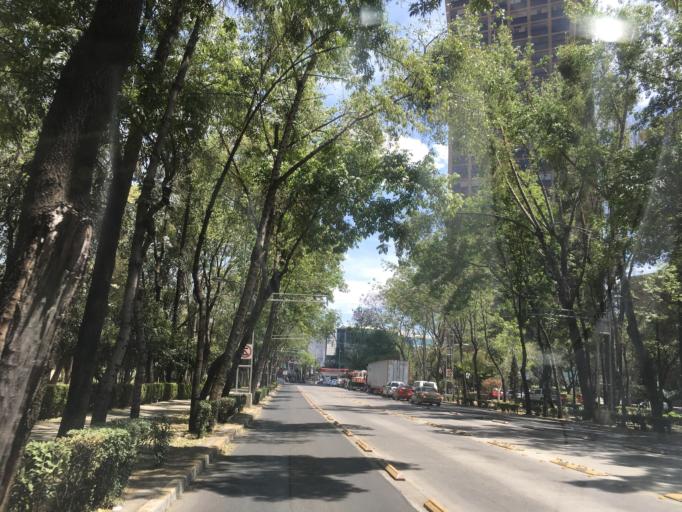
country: MX
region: Mexico City
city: Benito Juarez
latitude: 19.3978
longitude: -99.1661
